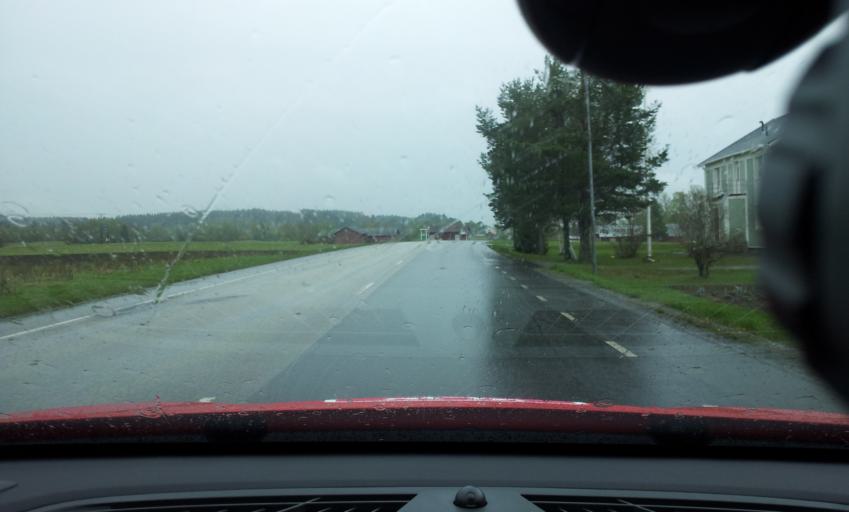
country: SE
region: Jaemtland
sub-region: OEstersunds Kommun
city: Brunflo
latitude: 63.1247
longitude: 14.7785
